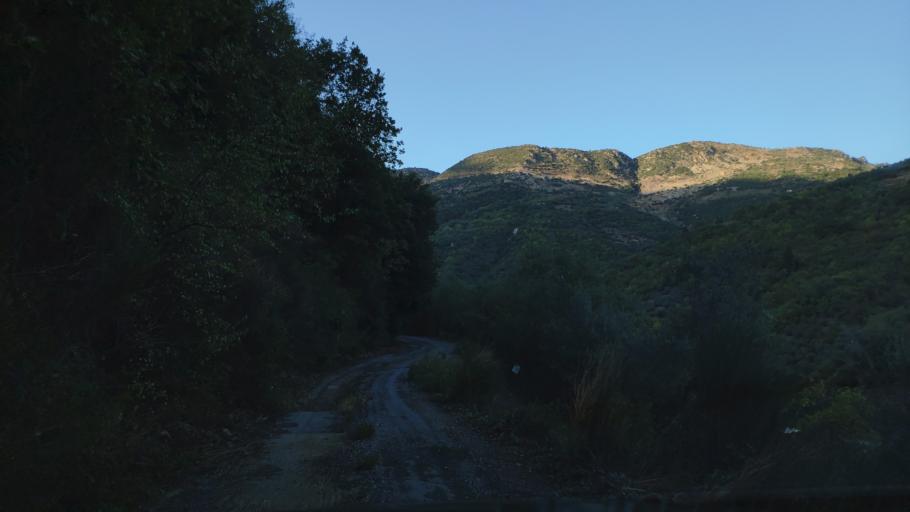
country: GR
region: Peloponnese
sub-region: Nomos Arkadias
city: Dimitsana
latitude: 37.5676
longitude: 22.0421
